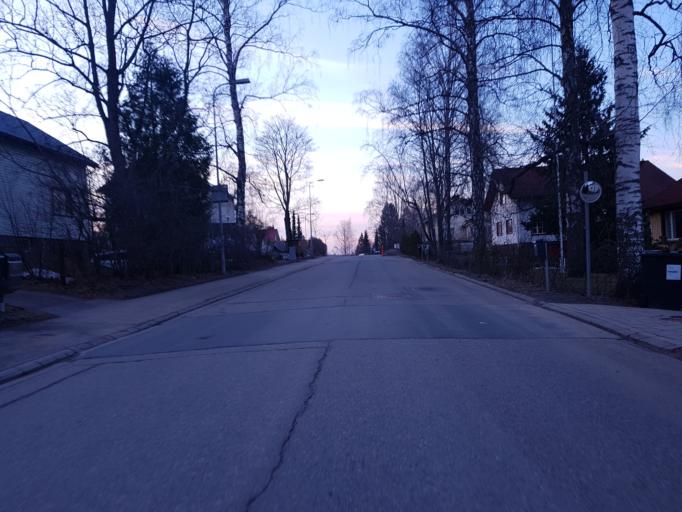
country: FI
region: Uusimaa
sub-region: Helsinki
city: Helsinki
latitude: 60.2603
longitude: 24.9531
